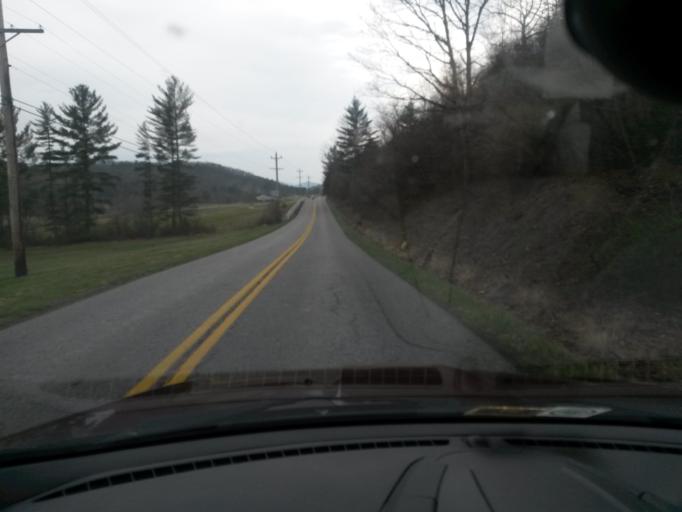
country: US
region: Virginia
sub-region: Bath County
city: Warm Springs
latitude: 37.9913
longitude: -79.8953
